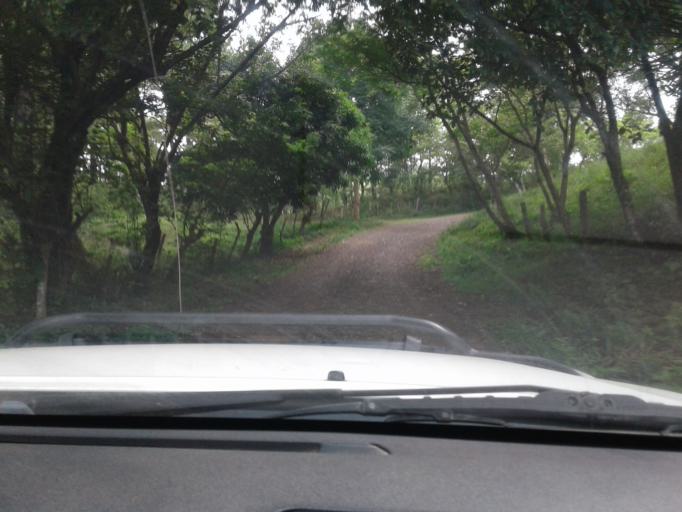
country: NI
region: Matagalpa
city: San Ramon
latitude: 12.9156
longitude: -85.7306
